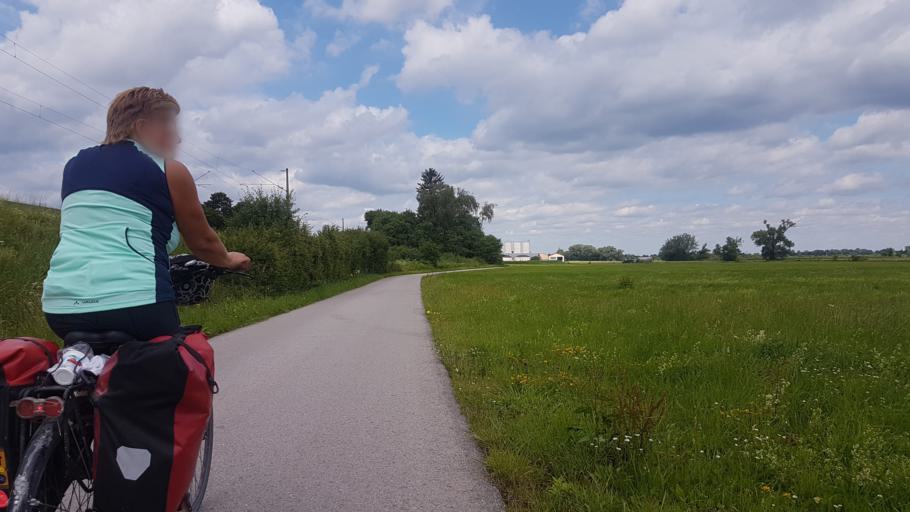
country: DE
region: Bavaria
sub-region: Regierungsbezirk Mittelfranken
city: Gunzenhausen
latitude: 49.0868
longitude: 10.7672
